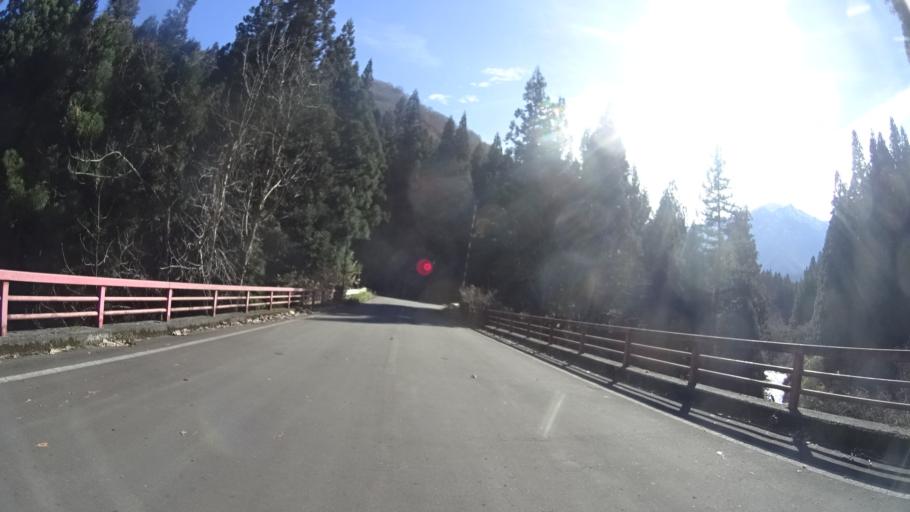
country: JP
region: Niigata
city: Muikamachi
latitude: 37.1769
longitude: 139.0865
